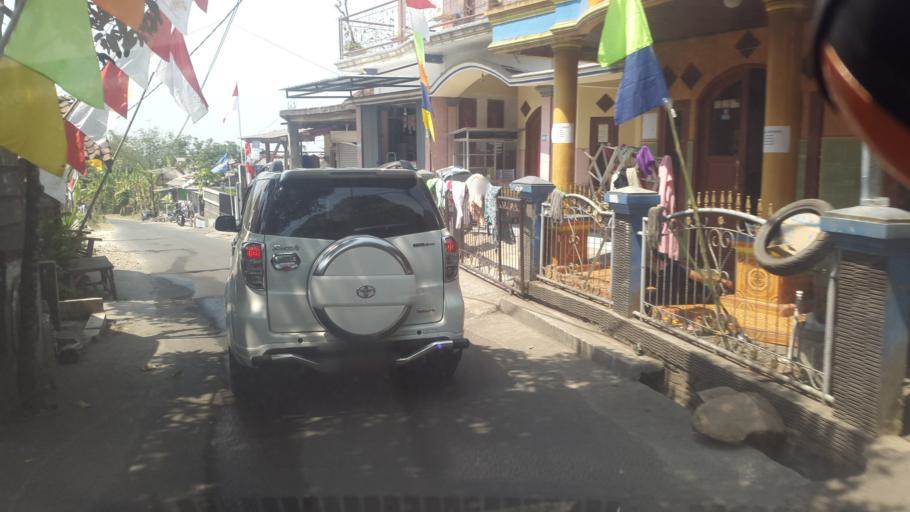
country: ID
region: West Java
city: Cicurug
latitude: -6.7800
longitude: 106.7439
